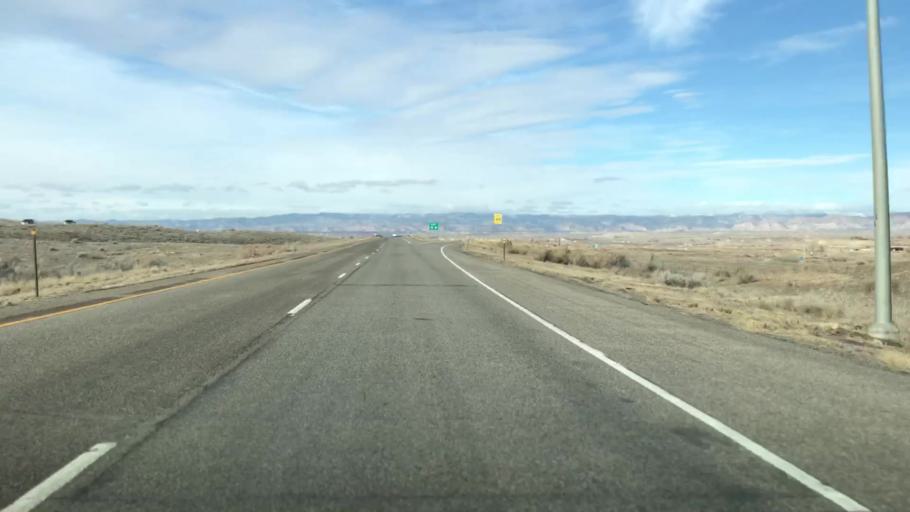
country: US
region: Colorado
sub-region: Mesa County
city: Loma
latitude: 39.2114
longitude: -108.8640
